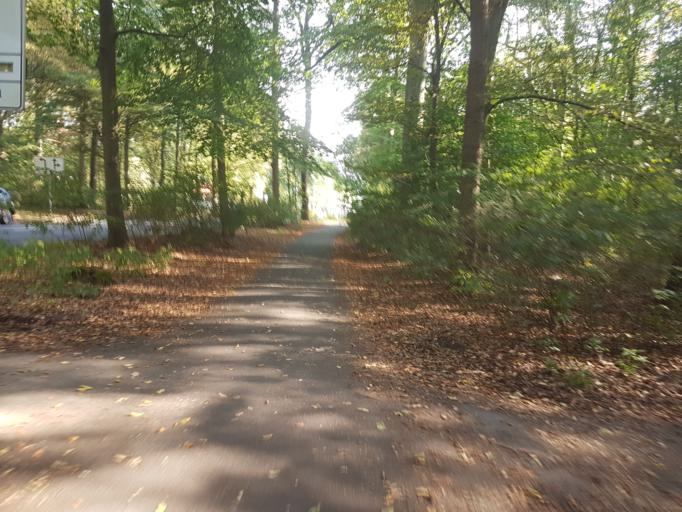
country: DE
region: Lower Saxony
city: Hannover
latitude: 52.3832
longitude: 9.7652
